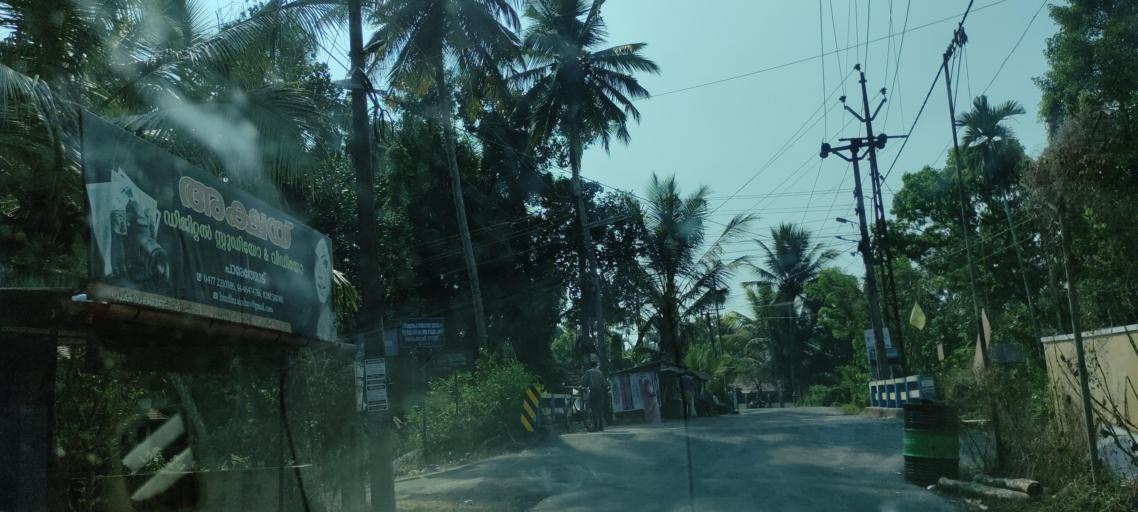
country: IN
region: Kerala
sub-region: Pattanamtitta
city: Tiruvalla
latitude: 9.3604
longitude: 76.4945
